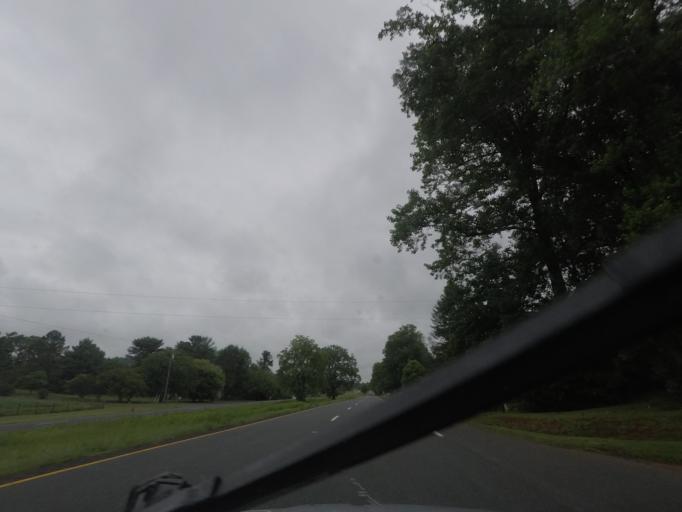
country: US
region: Virginia
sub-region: Orange County
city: Orange
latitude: 38.2115
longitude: -78.1348
